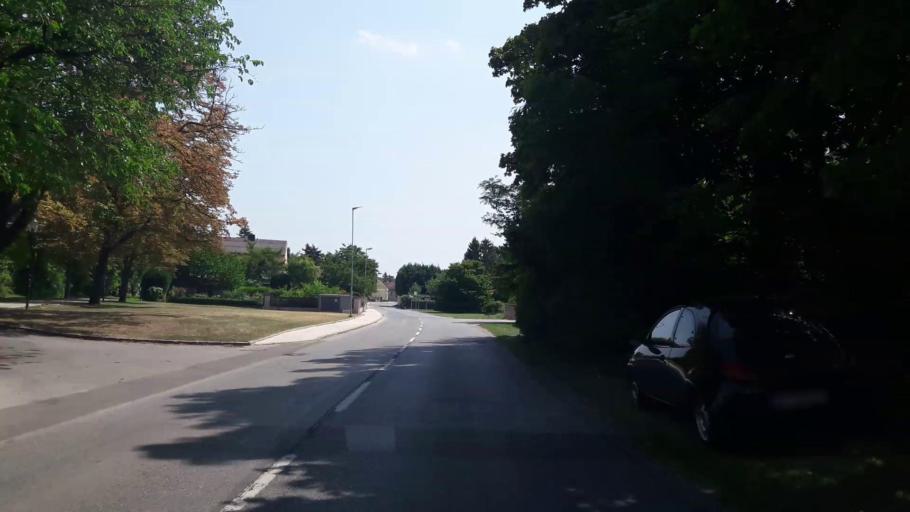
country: AT
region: Lower Austria
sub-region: Politischer Bezirk Bruck an der Leitha
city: Trautmannsdorf an der Leitha
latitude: 48.0232
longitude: 16.6437
